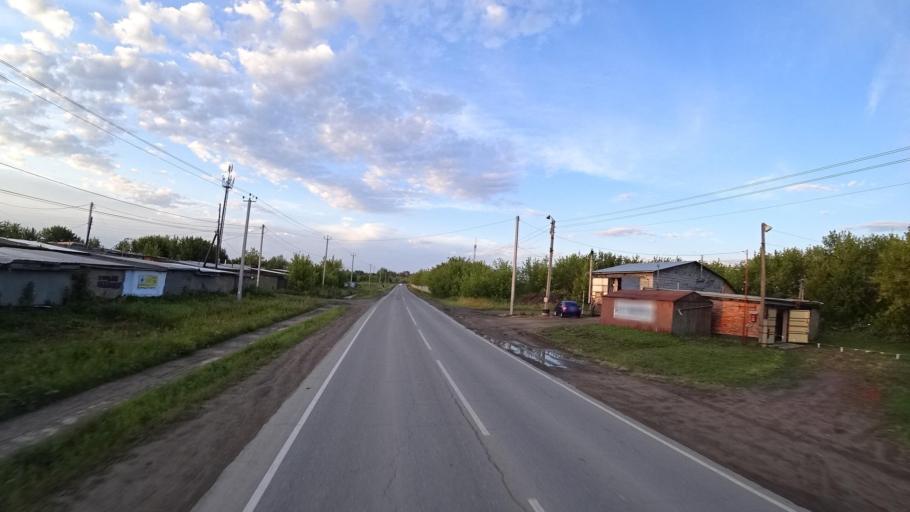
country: RU
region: Sverdlovsk
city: Kamyshlov
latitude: 56.8553
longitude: 62.7199
